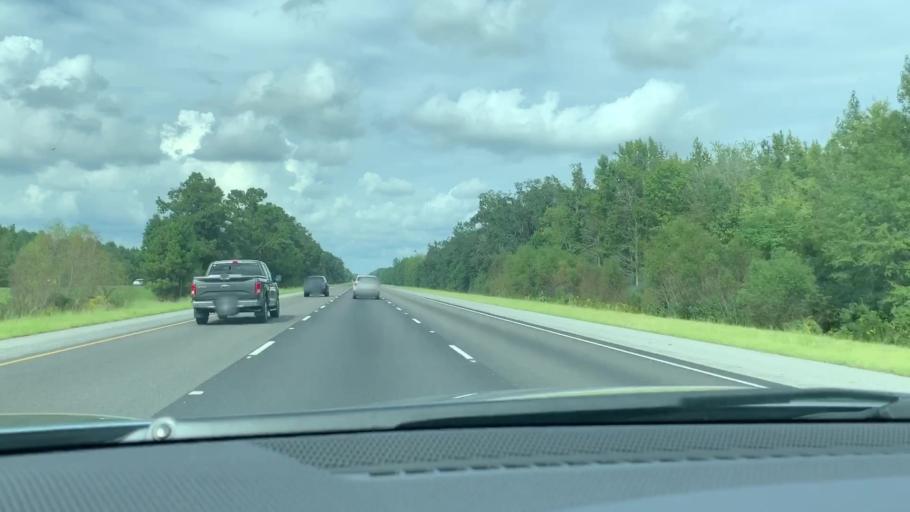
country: US
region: Georgia
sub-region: Liberty County
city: Midway
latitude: 31.6817
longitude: -81.3916
